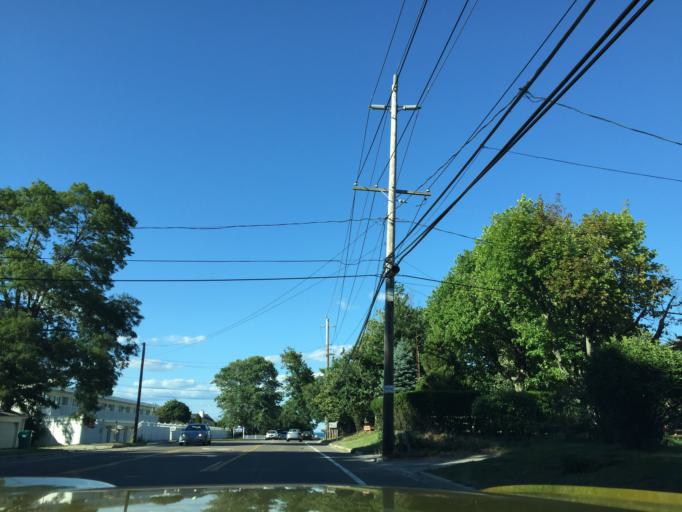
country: US
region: New York
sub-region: Suffolk County
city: Southold
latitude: 41.0862
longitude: -72.4167
